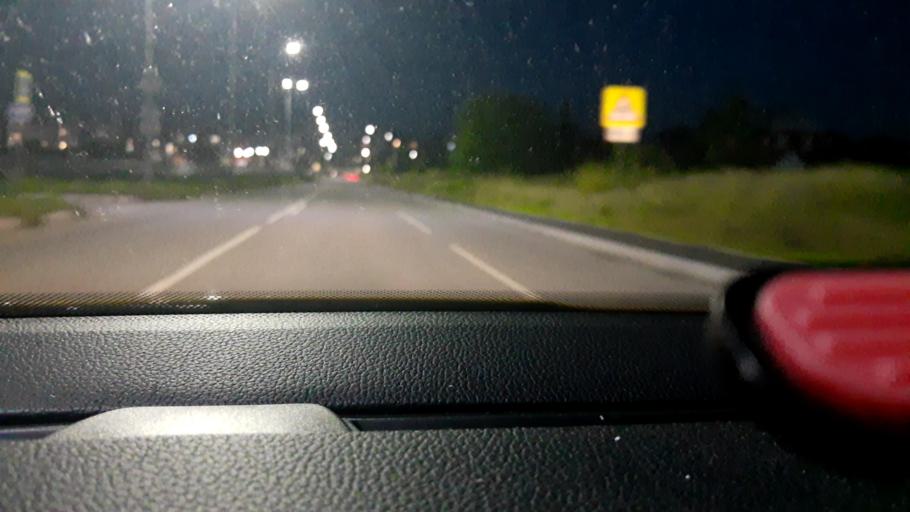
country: RU
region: Moskovskaya
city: Pirogovskiy
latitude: 55.9572
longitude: 37.6749
